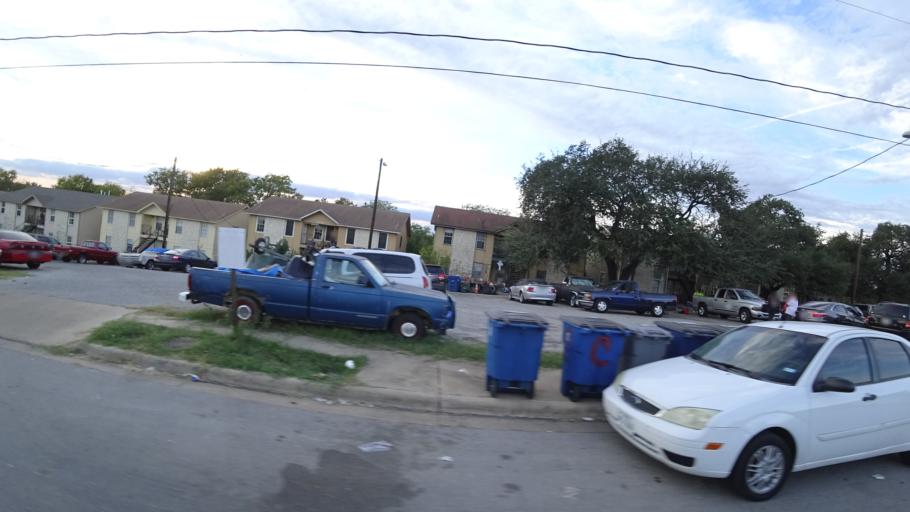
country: US
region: Texas
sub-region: Travis County
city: Austin
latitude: 30.2062
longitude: -97.7619
